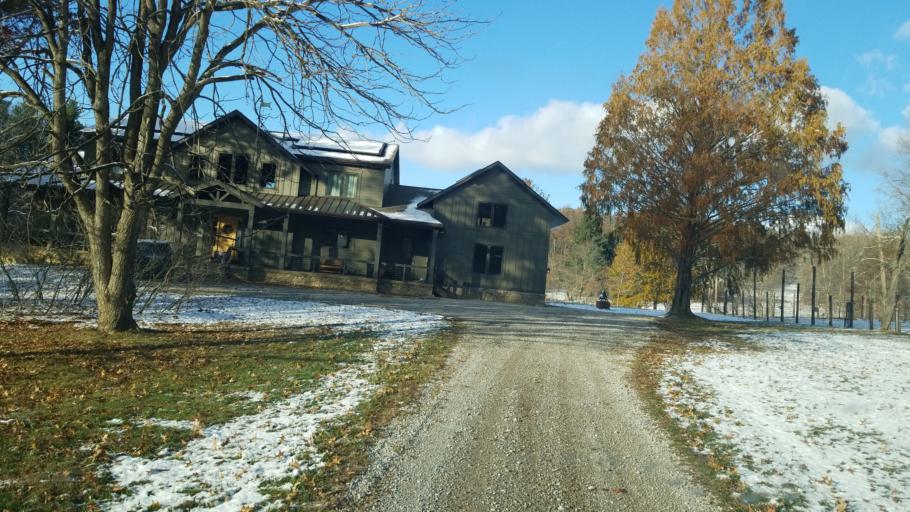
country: US
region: Ohio
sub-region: Licking County
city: Newark
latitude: 40.1542
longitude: -82.3861
